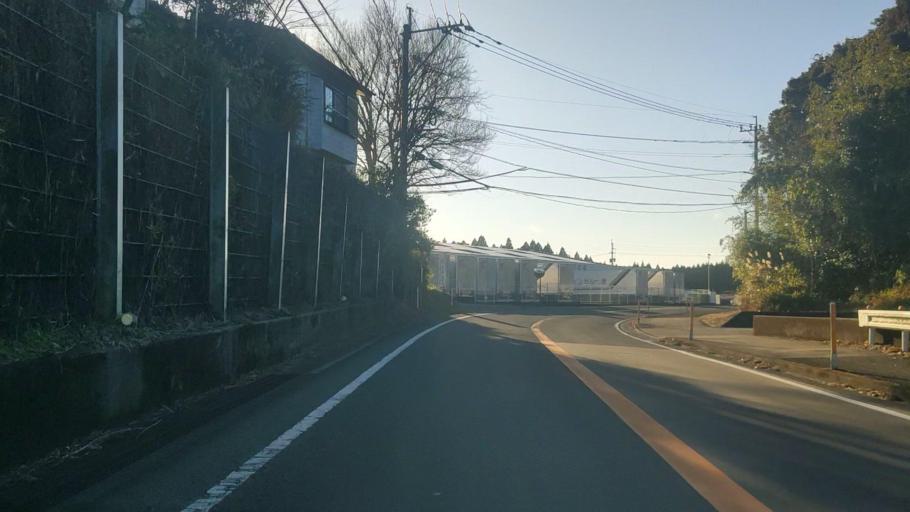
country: JP
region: Miyazaki
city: Miyazaki-shi
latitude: 31.8579
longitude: 131.3803
